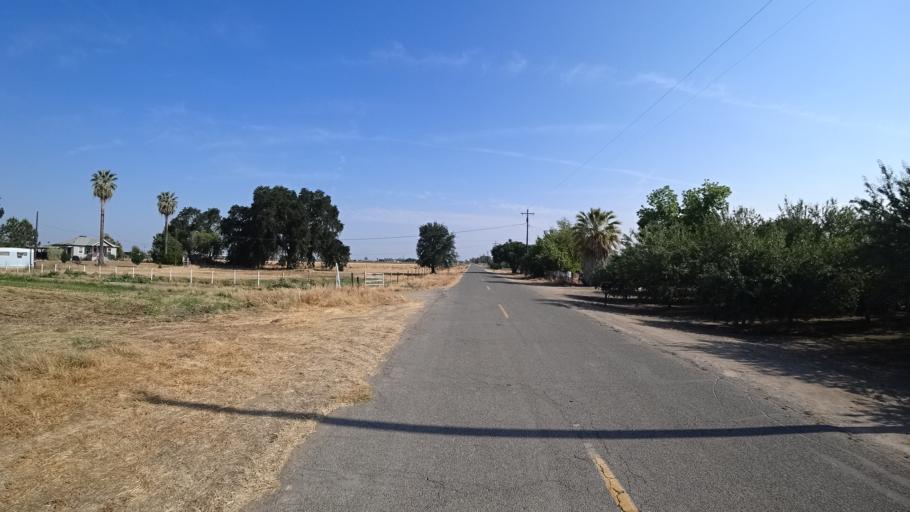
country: US
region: California
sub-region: Fresno County
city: Riverdale
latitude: 36.3711
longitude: -119.8341
